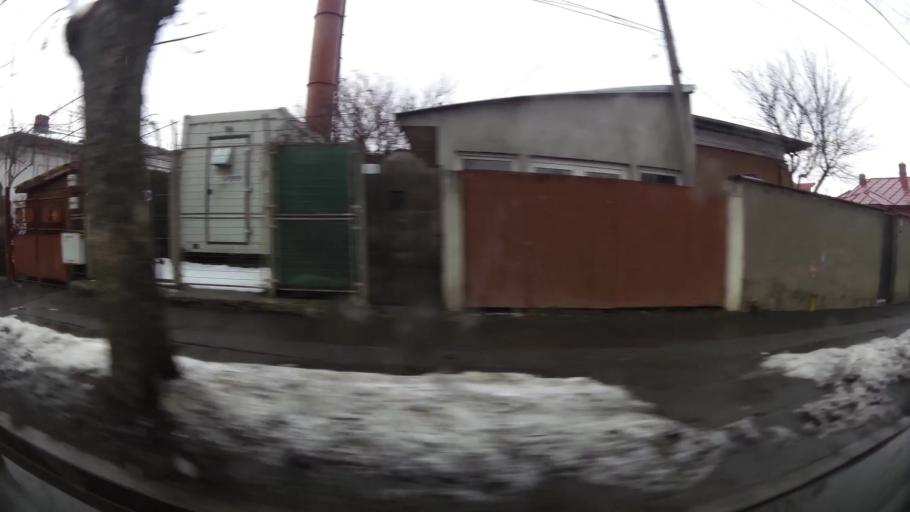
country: RO
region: Ilfov
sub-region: Comuna Chiajna
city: Rosu
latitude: 44.4927
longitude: 26.0286
